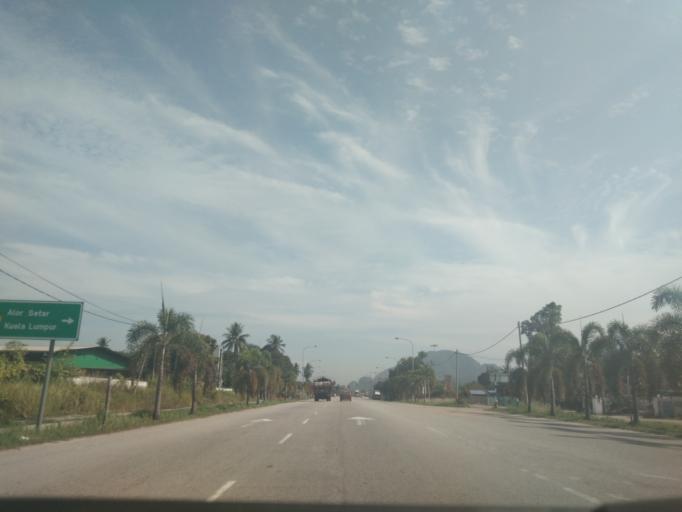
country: MY
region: Perak
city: Ipoh
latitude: 4.5222
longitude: 101.1334
